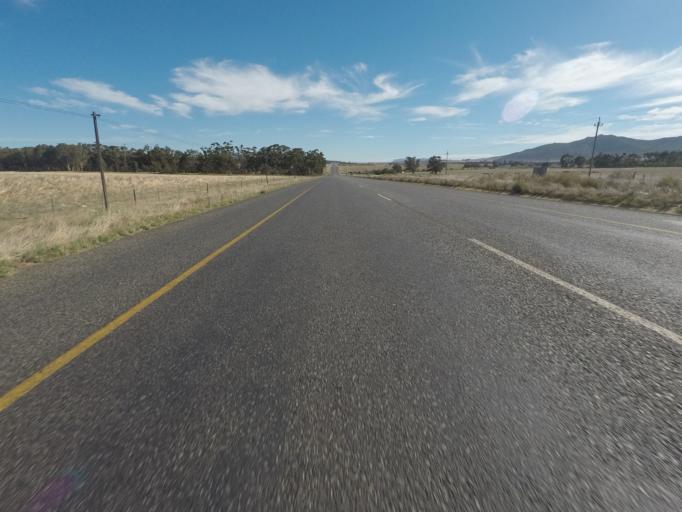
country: ZA
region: Western Cape
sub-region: West Coast District Municipality
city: Malmesbury
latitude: -33.6186
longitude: 18.7264
